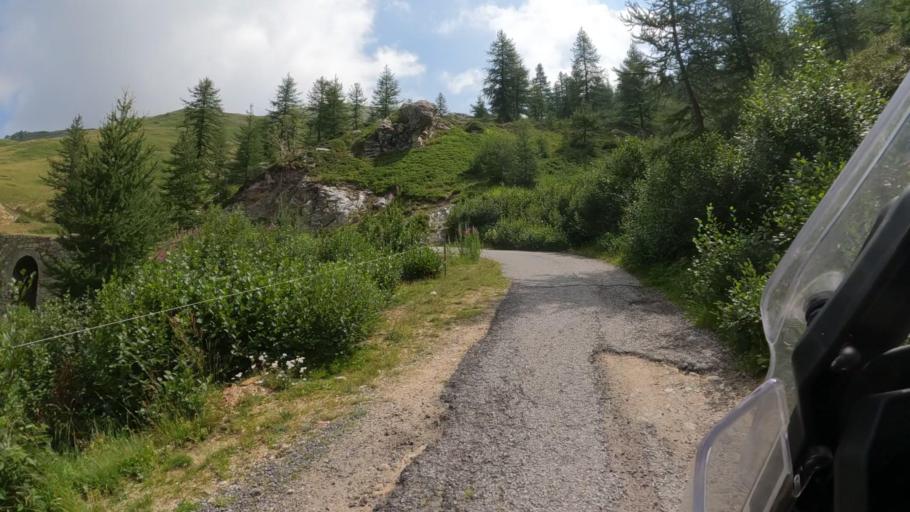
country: IT
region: Piedmont
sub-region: Provincia di Cuneo
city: Marmora
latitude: 44.3994
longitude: 7.1145
